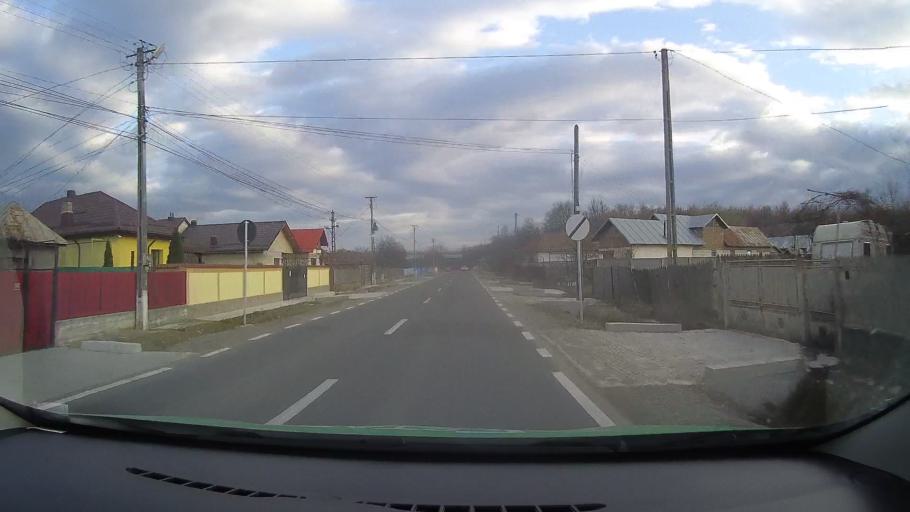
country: RO
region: Dambovita
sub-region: Comuna I. L. Caragiale
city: Mija
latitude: 44.9188
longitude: 25.6886
